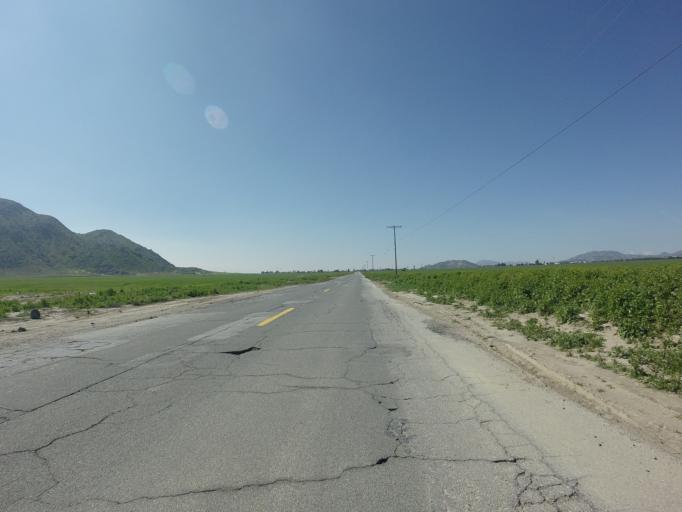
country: US
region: California
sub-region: Riverside County
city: Lakeview
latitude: 33.9195
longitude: -117.1288
